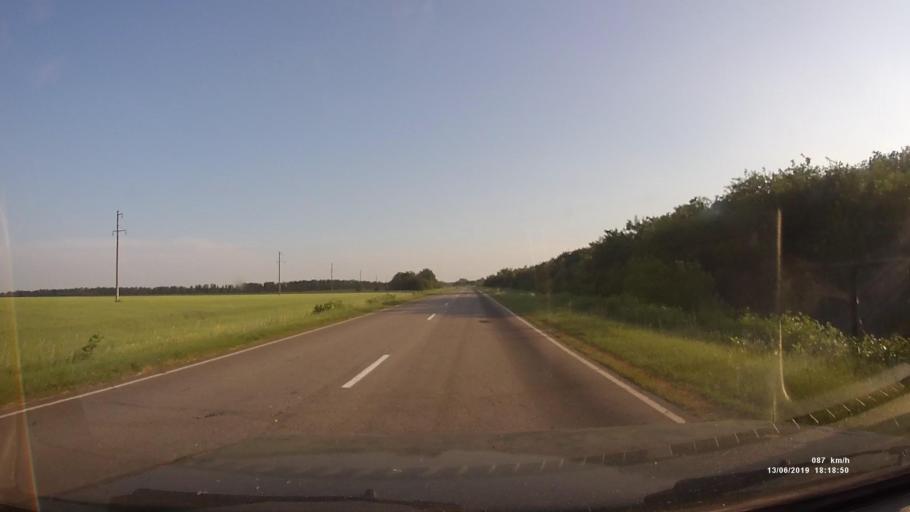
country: RU
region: Rostov
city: Kazanskaya
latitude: 49.9035
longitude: 41.3104
